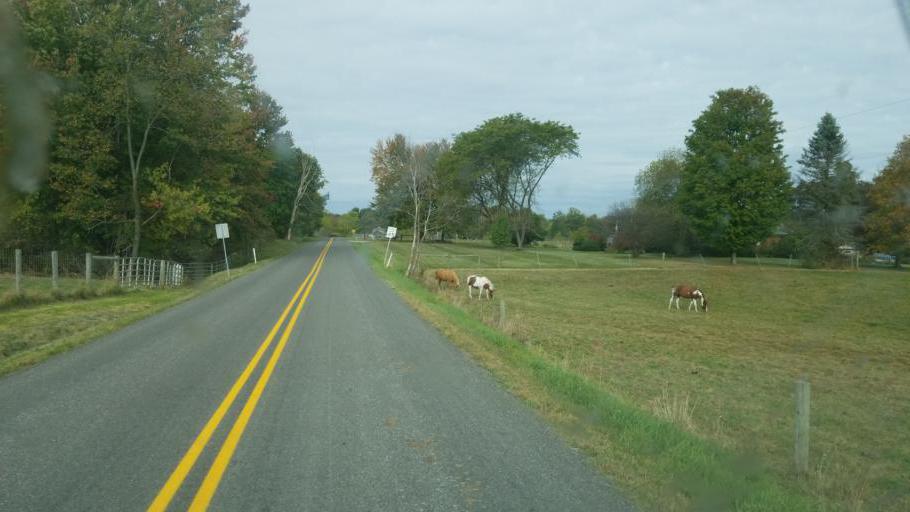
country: US
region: Pennsylvania
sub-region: Mercer County
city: Mercer
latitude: 41.3384
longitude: -80.2670
